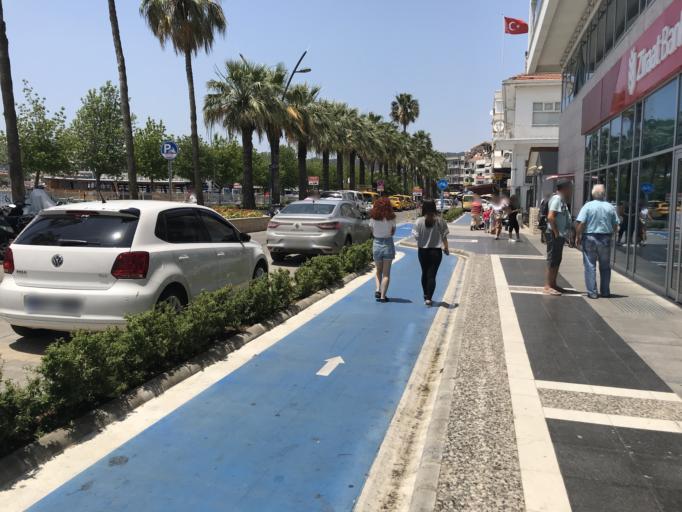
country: TR
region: Mugla
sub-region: Marmaris
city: Marmaris
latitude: 36.8520
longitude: 28.2731
